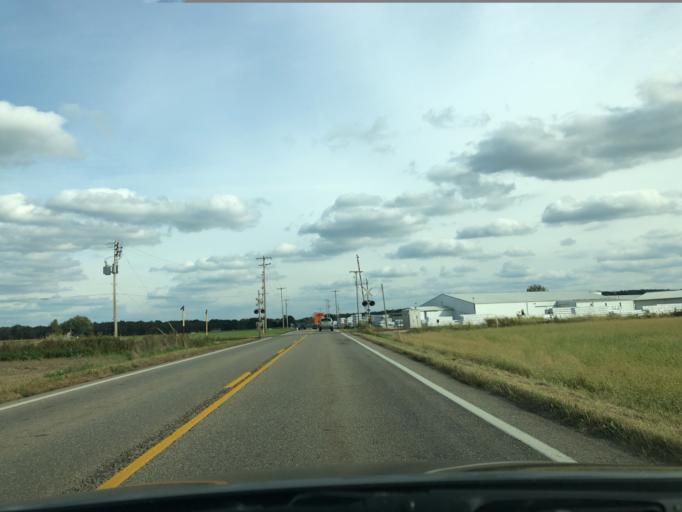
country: US
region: Ohio
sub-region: Stark County
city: Beach City
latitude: 40.6436
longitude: -81.5848
